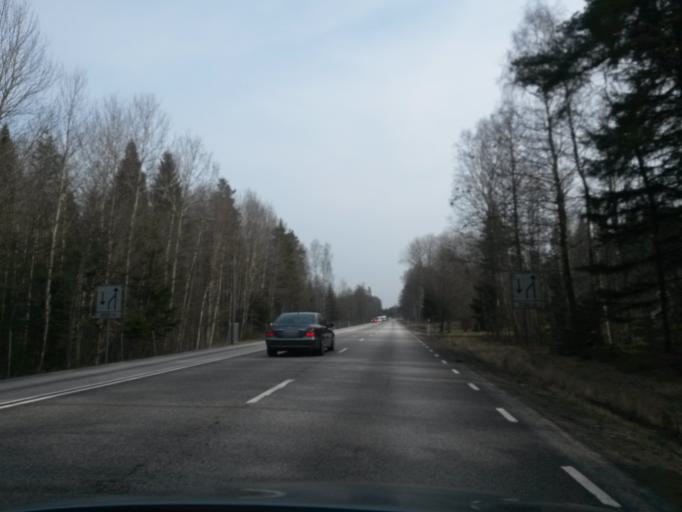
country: SE
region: Vaestra Goetaland
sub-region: Gullspangs Kommun
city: Anderstorp
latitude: 58.8765
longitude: 14.2624
